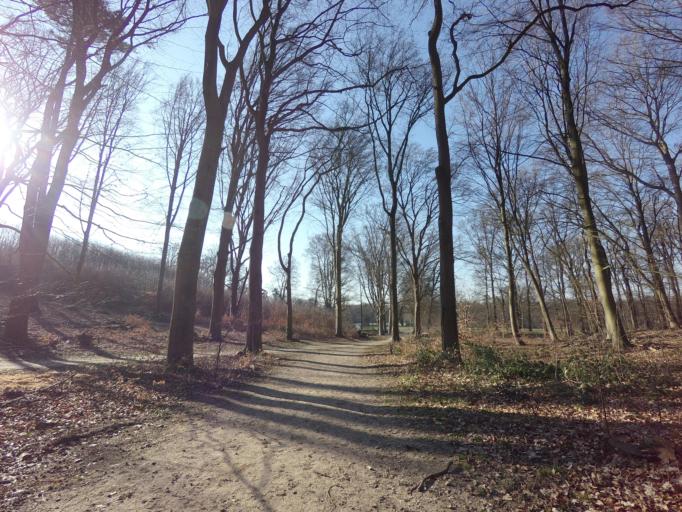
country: NL
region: Gelderland
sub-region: Gemeente Lochem
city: Barchem
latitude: 52.1401
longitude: 6.4265
